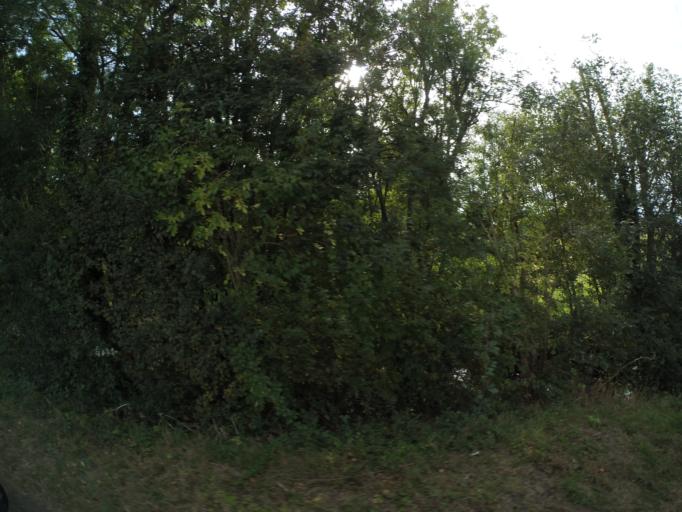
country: FR
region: Pays de la Loire
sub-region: Departement de Maine-et-Loire
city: Jallais
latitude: 47.1941
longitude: -0.8893
